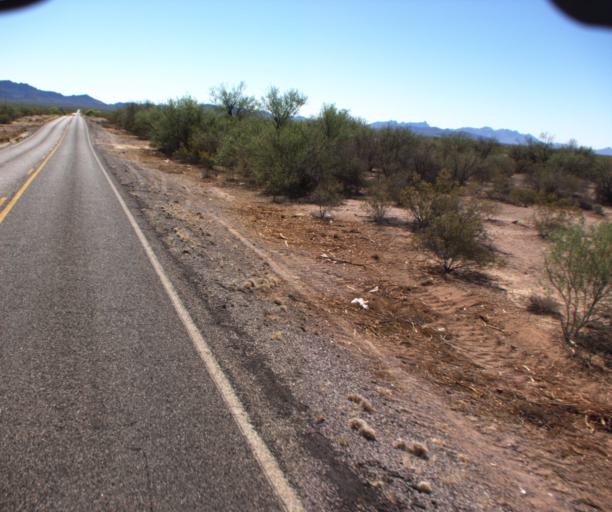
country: US
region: Arizona
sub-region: Pima County
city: Ajo
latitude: 32.3423
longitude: -112.8039
